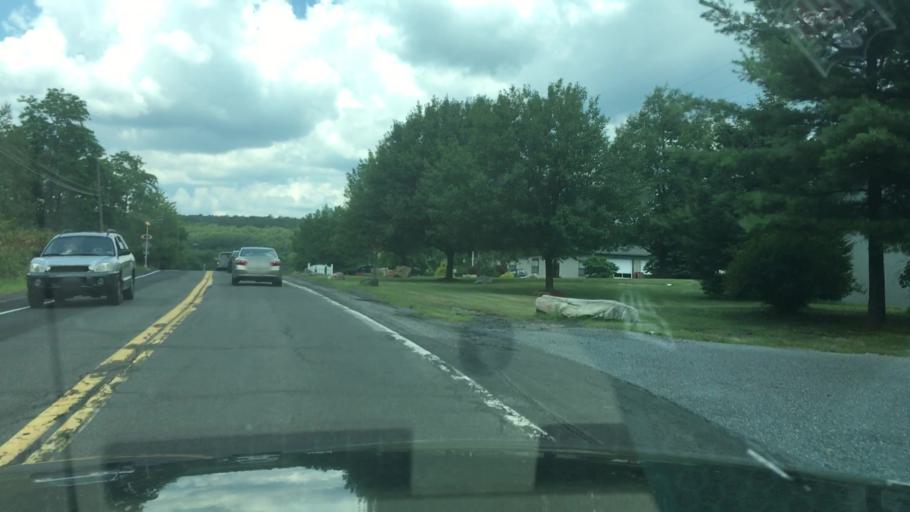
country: US
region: Pennsylvania
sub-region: Schuylkill County
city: Minersville
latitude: 40.7070
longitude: -76.3292
